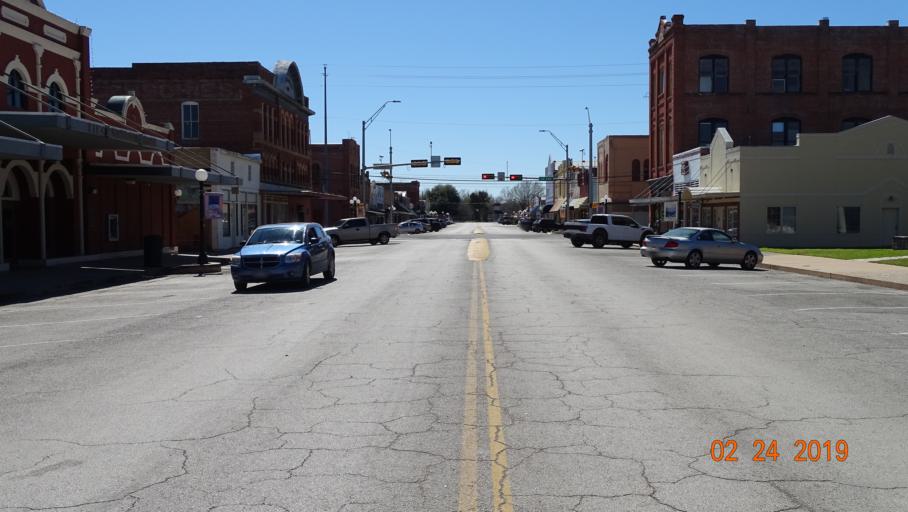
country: US
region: Texas
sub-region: Bastrop County
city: Smithville
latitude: 30.0091
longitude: -97.1593
